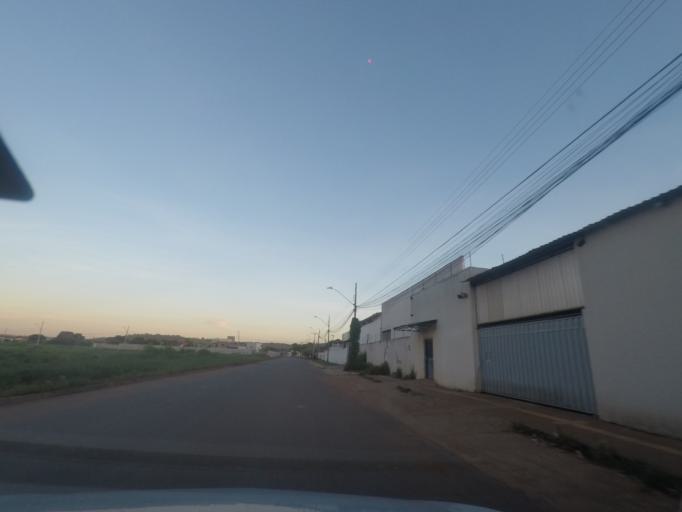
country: BR
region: Goias
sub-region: Goiania
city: Goiania
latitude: -16.6930
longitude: -49.3337
